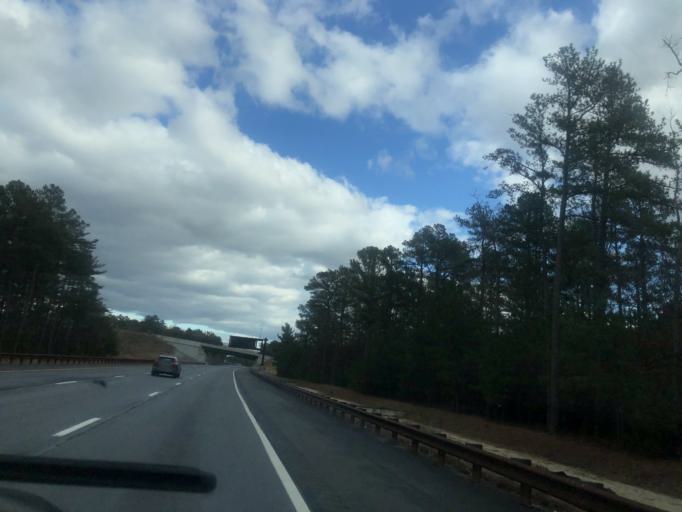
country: US
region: New Jersey
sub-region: Ocean County
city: Tuckerton
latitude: 39.6167
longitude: -74.4149
